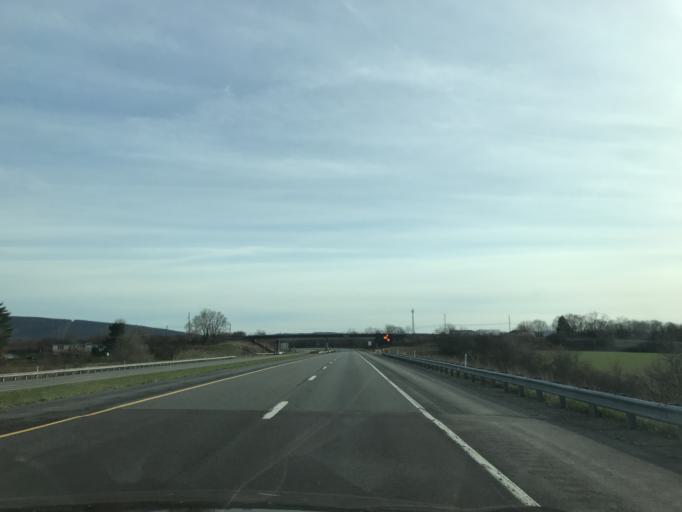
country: US
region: Pennsylvania
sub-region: Northumberland County
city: Milton
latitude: 40.9991
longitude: -76.8345
